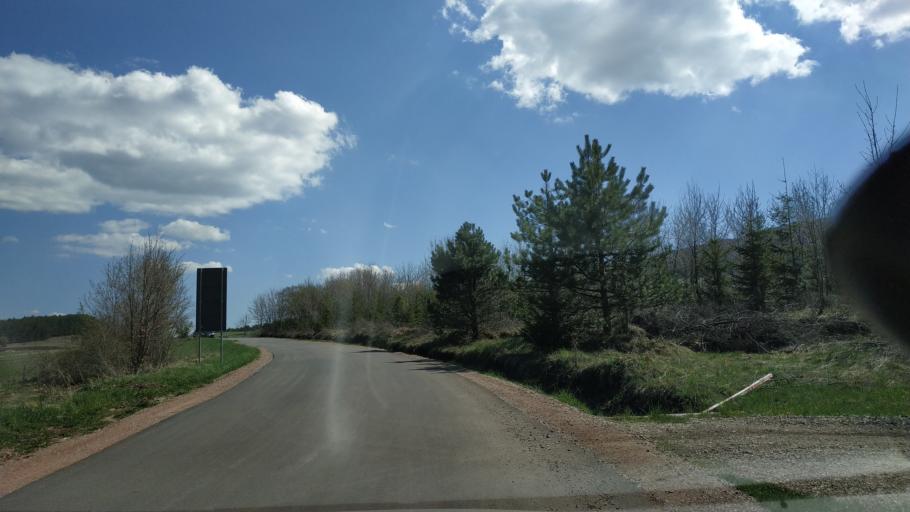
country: RS
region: Central Serbia
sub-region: Zajecarski Okrug
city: Soko Banja
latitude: 43.5968
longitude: 21.8829
